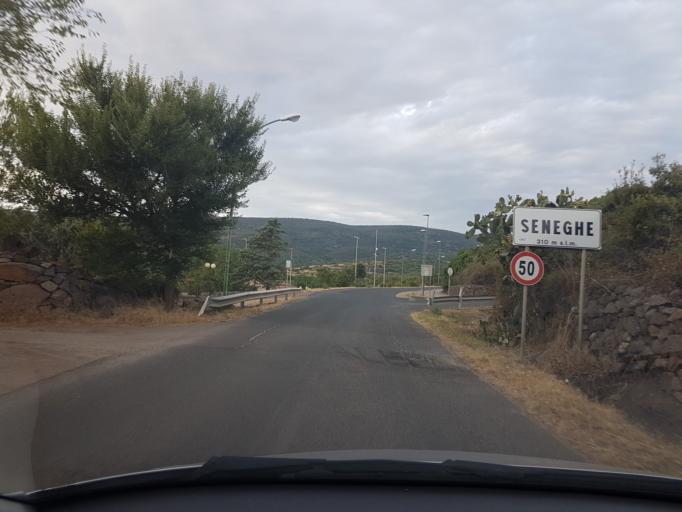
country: IT
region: Sardinia
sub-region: Provincia di Oristano
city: Seneghe
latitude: 40.0788
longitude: 8.6067
